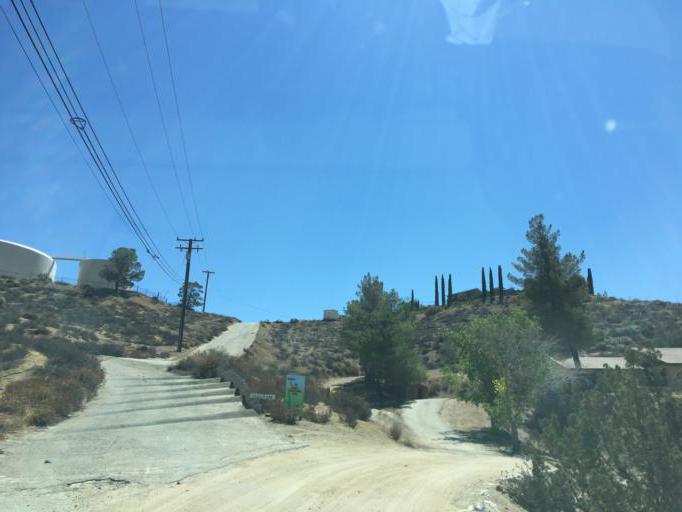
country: US
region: California
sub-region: Los Angeles County
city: Acton
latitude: 34.4736
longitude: -118.1786
